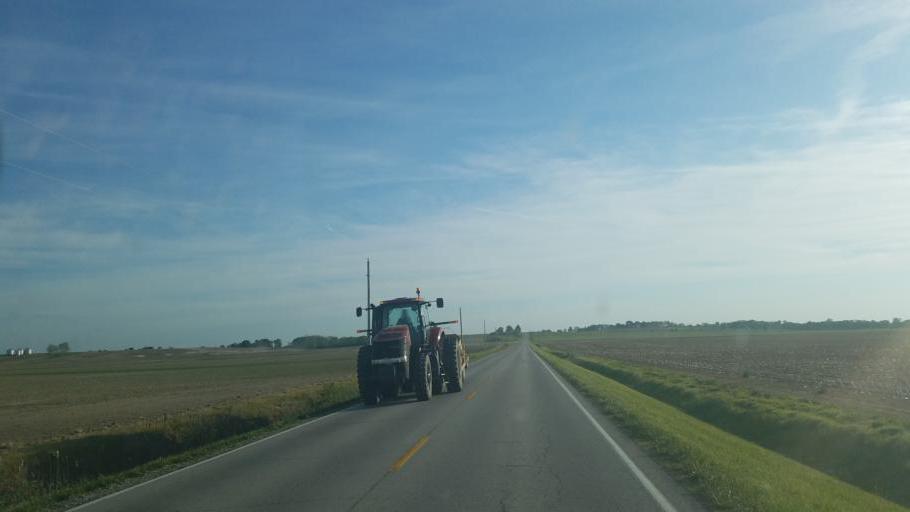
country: US
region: Ohio
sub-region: Highland County
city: Greenfield
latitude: 39.3797
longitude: -83.3437
